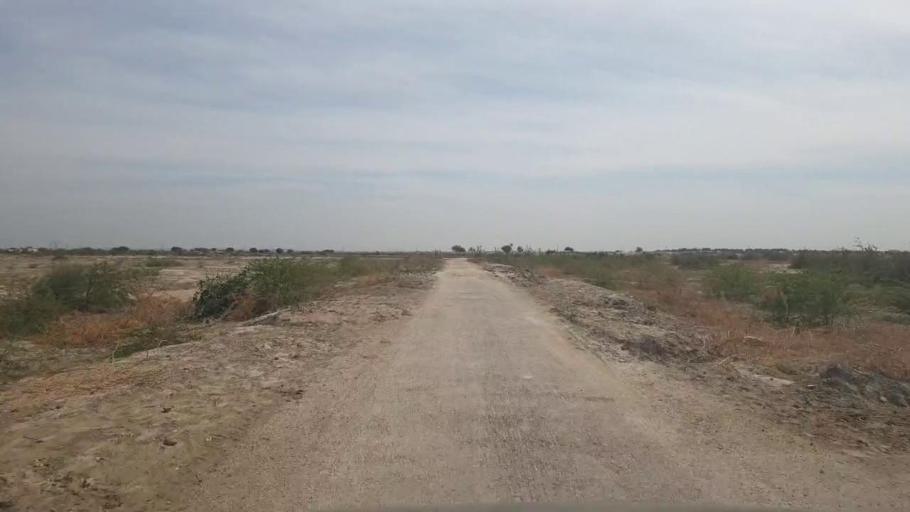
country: PK
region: Sindh
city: Kunri
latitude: 25.2153
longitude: 69.6231
